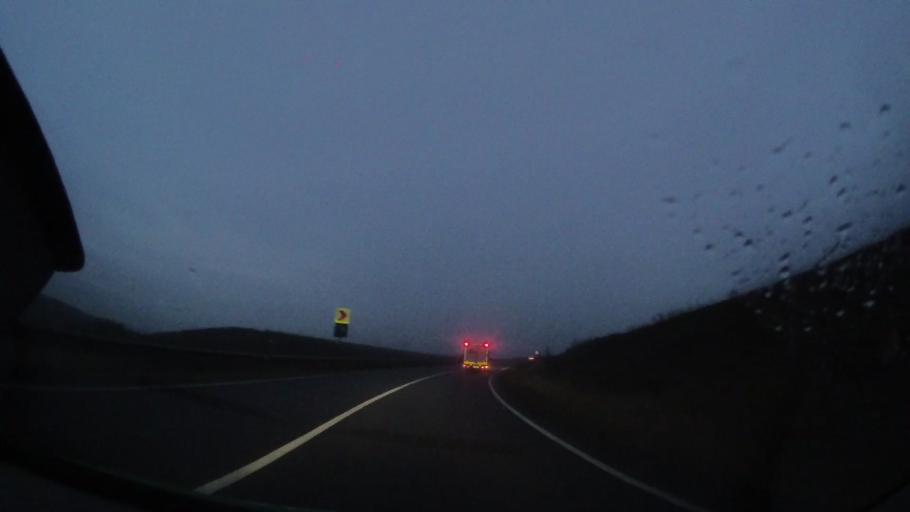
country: RO
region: Harghita
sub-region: Comuna Subcetate
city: Subcetate
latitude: 46.8404
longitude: 25.4796
